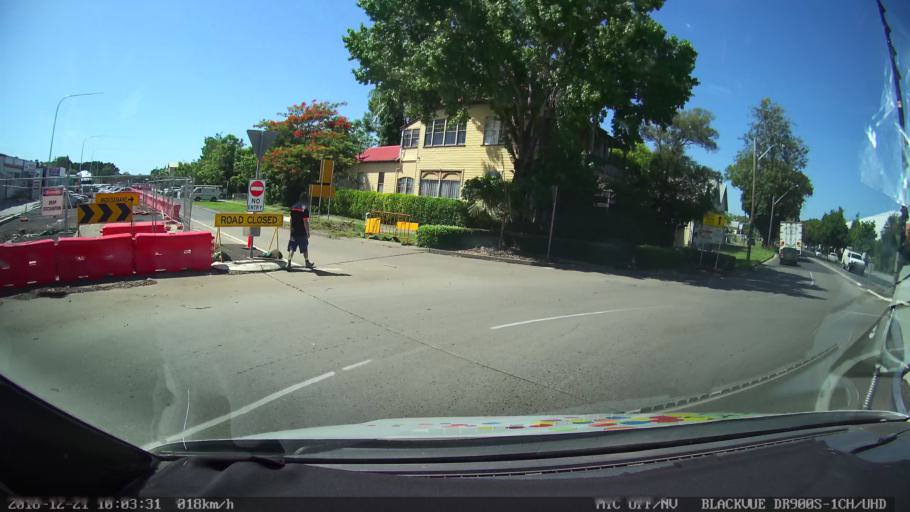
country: AU
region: New South Wales
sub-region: Clarence Valley
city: Grafton
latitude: -29.6916
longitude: 152.9385
